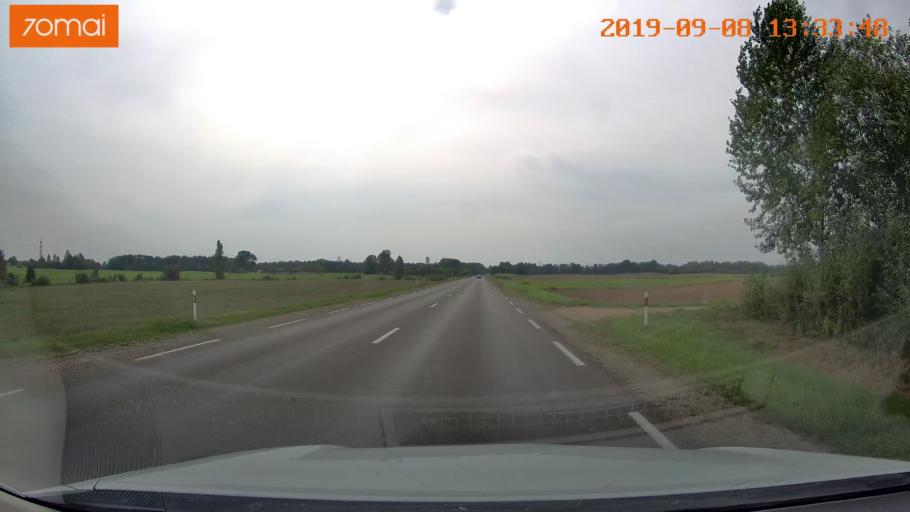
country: LT
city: Jieznas
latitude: 54.5031
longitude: 24.1326
